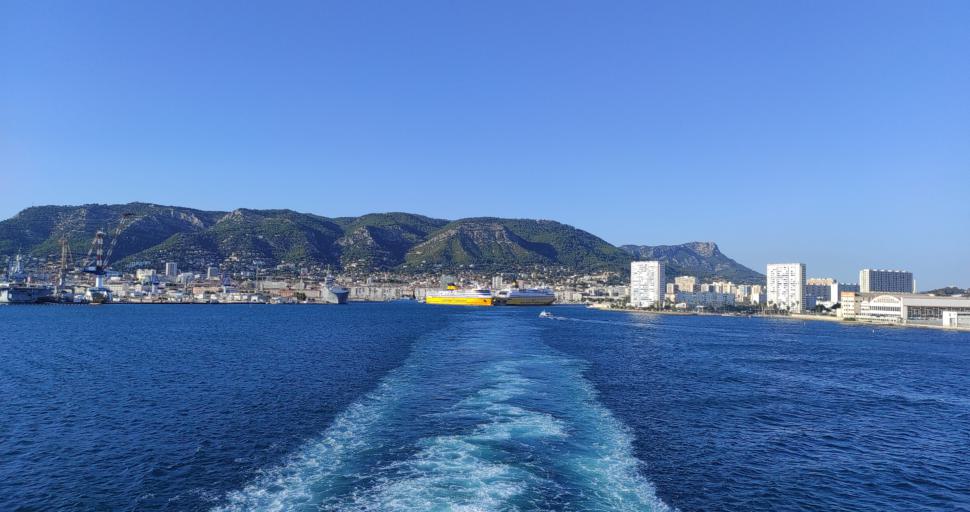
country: FR
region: Provence-Alpes-Cote d'Azur
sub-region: Departement du Var
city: Toulon
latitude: 43.1075
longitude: 5.9222
